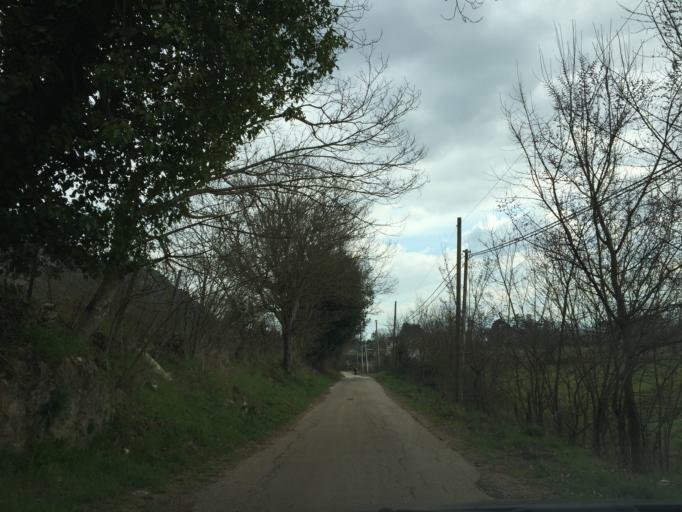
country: IT
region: Latium
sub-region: Provincia di Frosinone
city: Villa Santa Lucia
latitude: 41.4886
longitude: 13.7882
